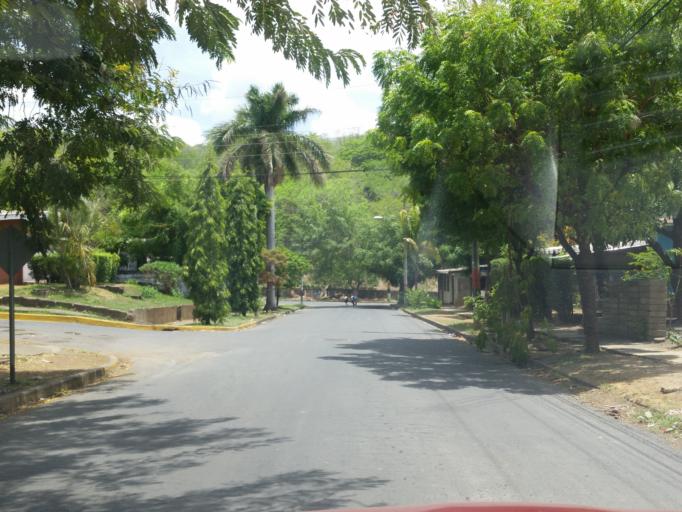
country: NI
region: Managua
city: Managua
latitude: 12.1025
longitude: -86.2738
